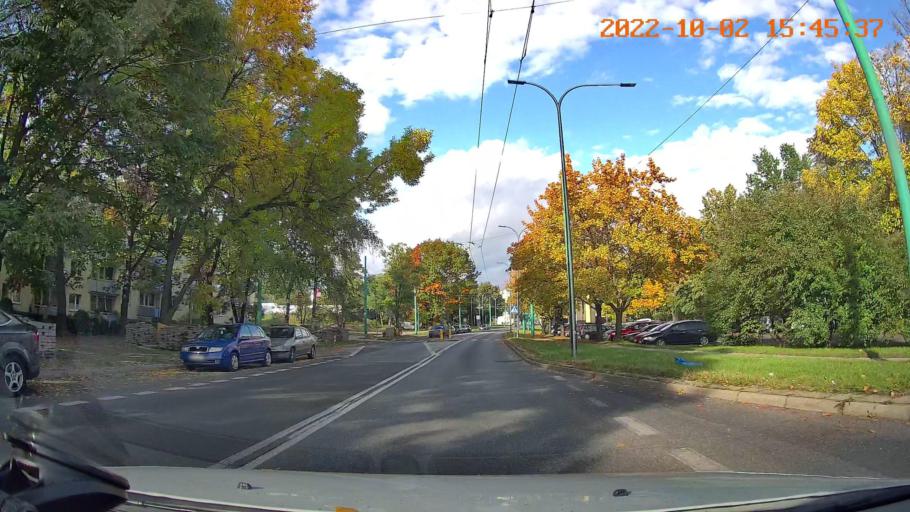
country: PL
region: Silesian Voivodeship
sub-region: Tychy
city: Cielmice
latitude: 50.1008
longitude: 18.9935
